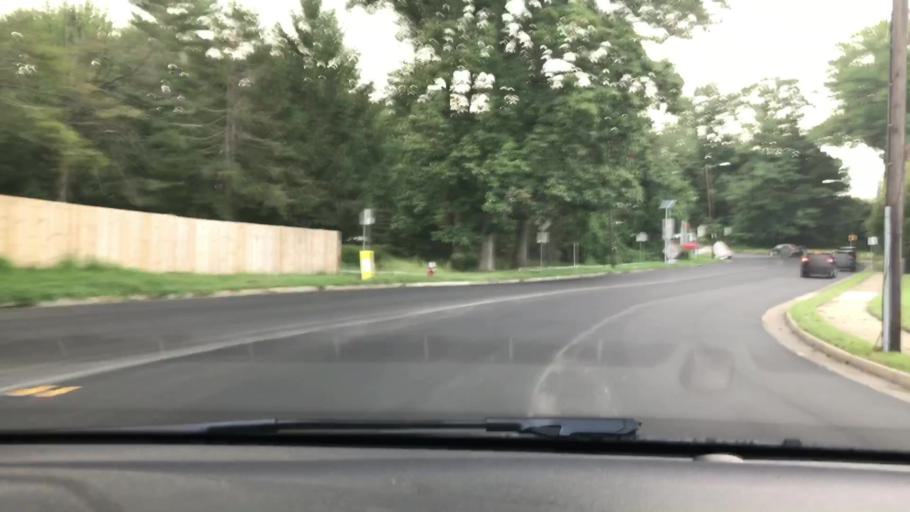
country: US
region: Virginia
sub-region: Fairfax County
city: Annandale
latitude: 38.8409
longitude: -77.1987
